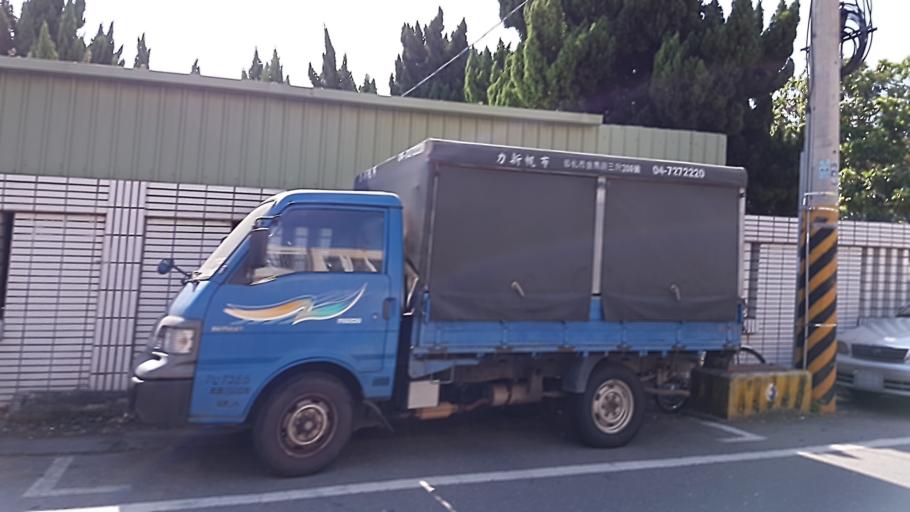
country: TW
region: Taiwan
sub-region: Changhua
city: Chang-hua
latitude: 24.0815
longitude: 120.4991
